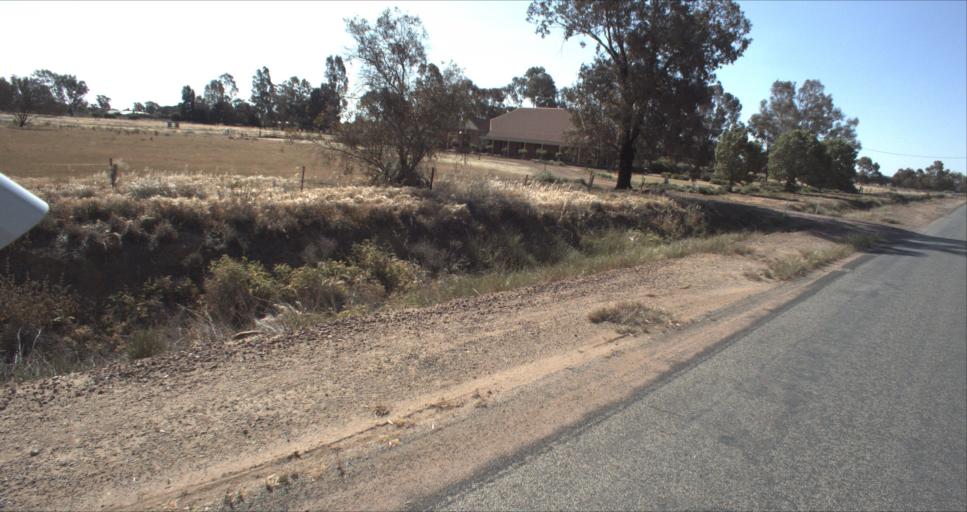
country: AU
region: New South Wales
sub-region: Leeton
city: Leeton
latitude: -34.5379
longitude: 146.4196
